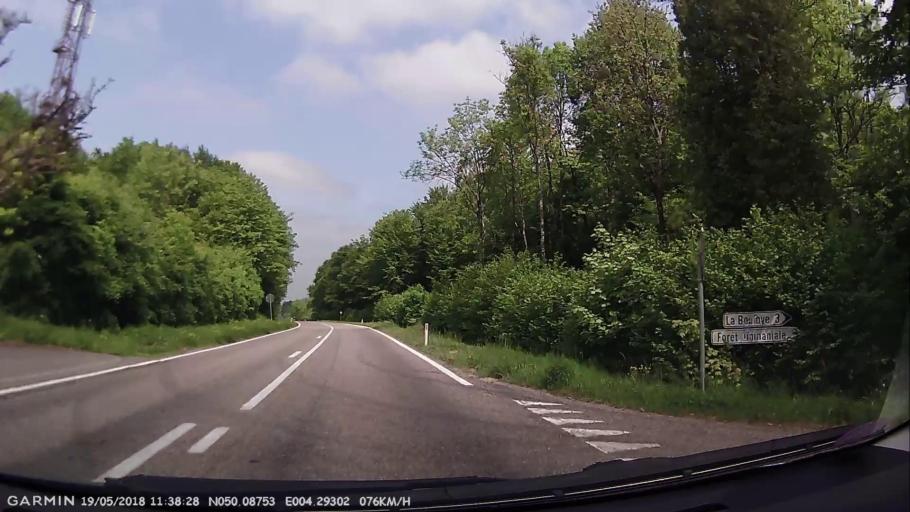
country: BE
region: Wallonia
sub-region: Province du Hainaut
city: Chimay
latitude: 50.0877
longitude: 4.2930
